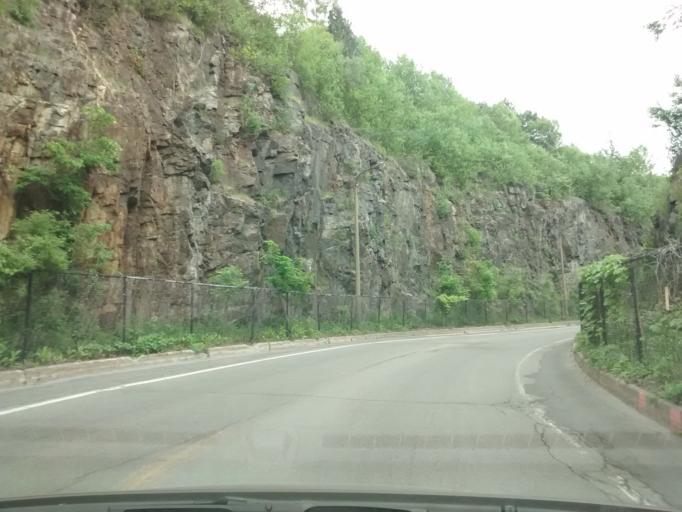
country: CA
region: Quebec
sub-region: Montreal
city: Montreal
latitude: 45.5098
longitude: -73.5917
